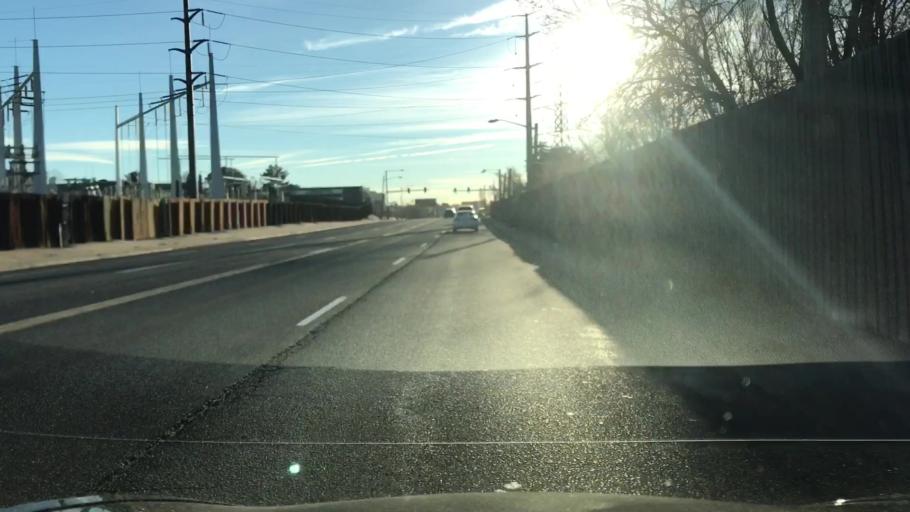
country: US
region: Colorado
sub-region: Arapahoe County
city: Glendale
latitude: 39.7062
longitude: -104.9193
